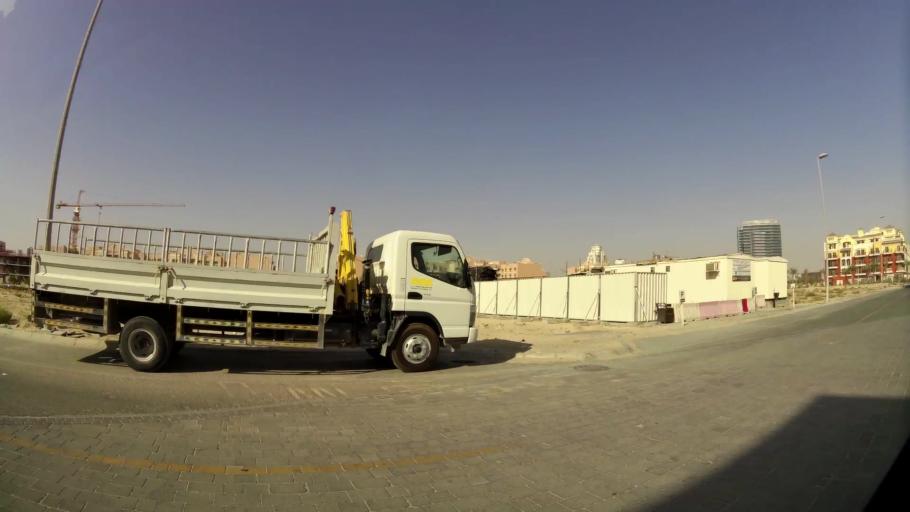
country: AE
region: Dubai
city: Dubai
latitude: 25.0520
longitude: 55.2121
